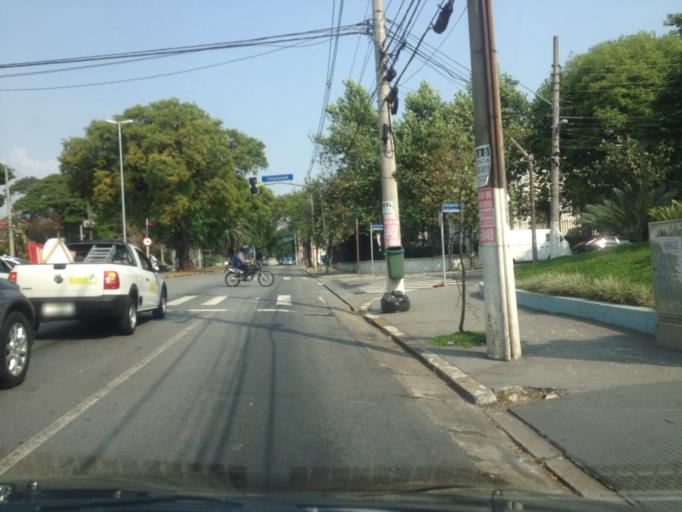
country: BR
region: Sao Paulo
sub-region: Sao Paulo
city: Sao Paulo
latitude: -23.5754
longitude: -46.6657
